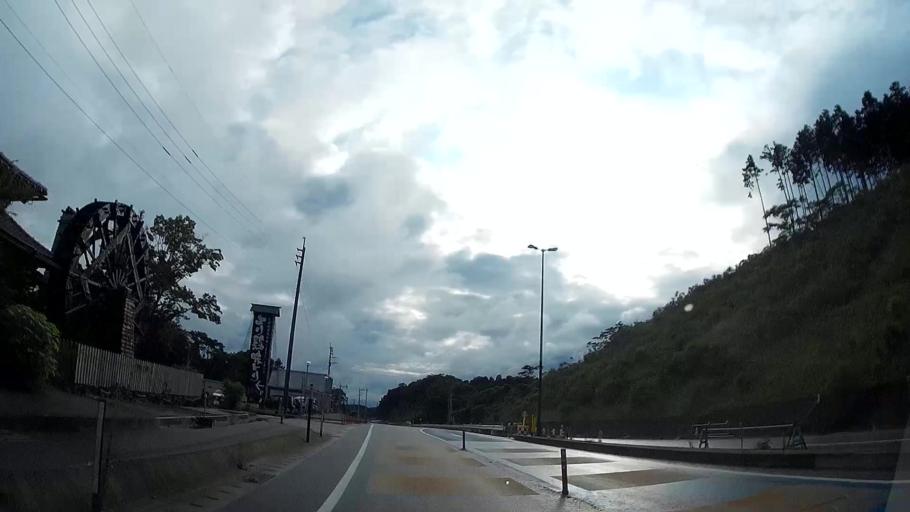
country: JP
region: Kumamoto
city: Ozu
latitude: 32.8768
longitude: 130.9428
